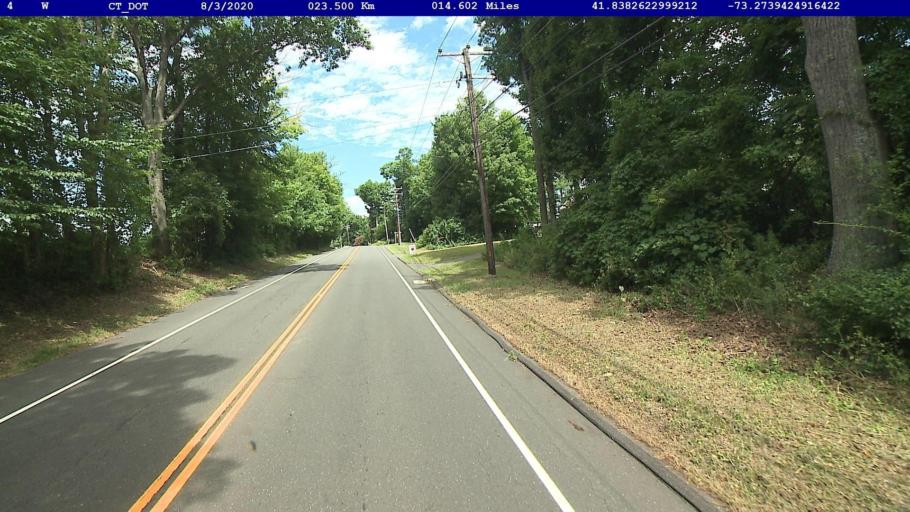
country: US
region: Connecticut
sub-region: Litchfield County
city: Litchfield
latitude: 41.8383
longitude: -73.2740
